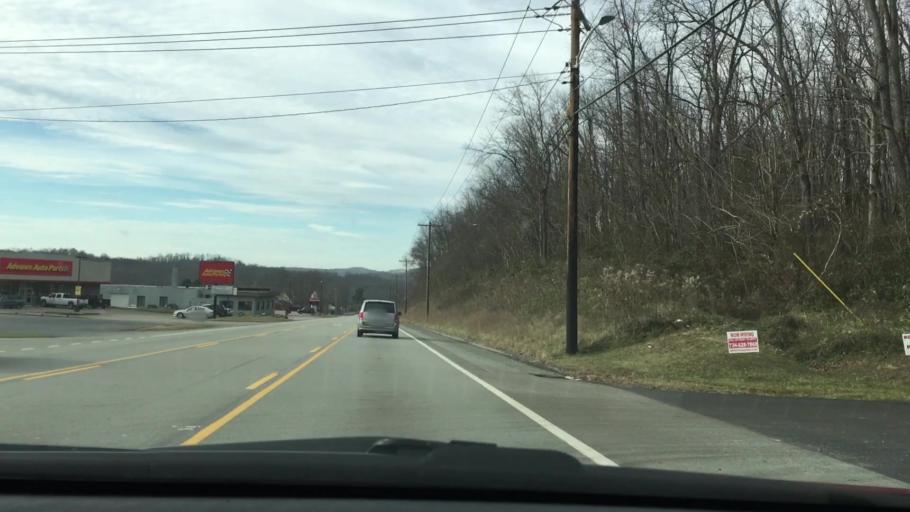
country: US
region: Pennsylvania
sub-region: Fayette County
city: Masontown
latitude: 39.8529
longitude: -79.9121
